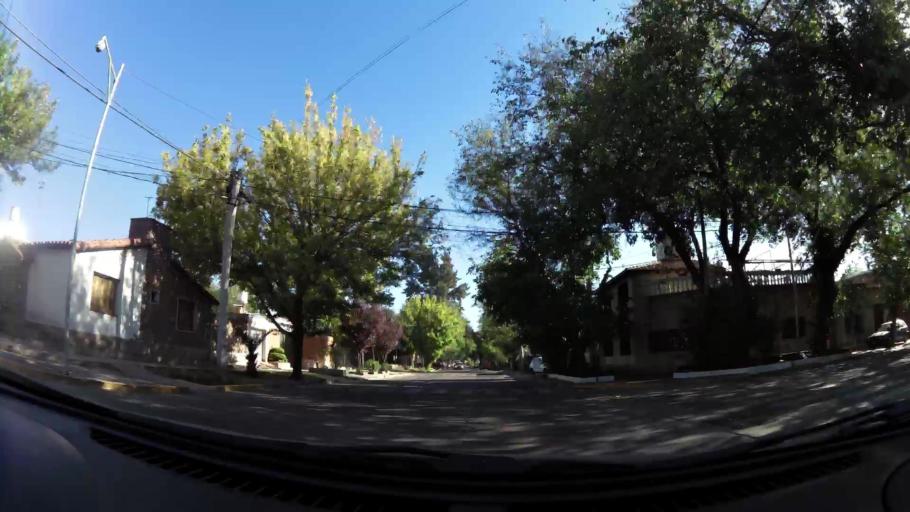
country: AR
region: Mendoza
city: Las Heras
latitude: -32.8637
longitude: -68.8438
